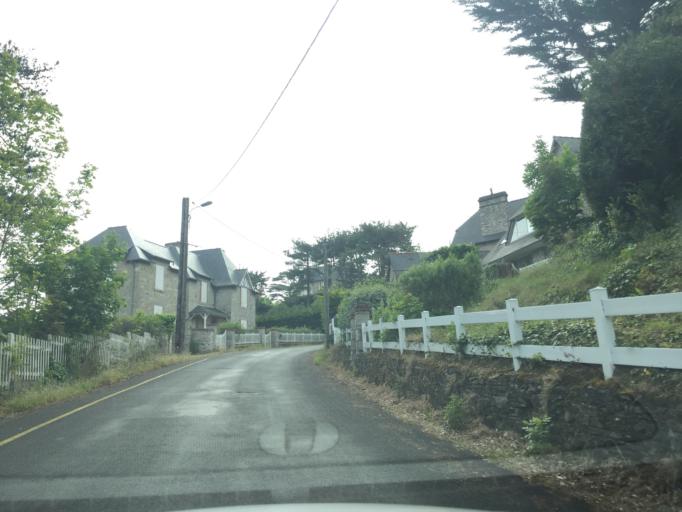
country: FR
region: Brittany
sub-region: Departement des Cotes-d'Armor
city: Saint-Cast-le-Guildo
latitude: 48.6230
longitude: -2.2451
